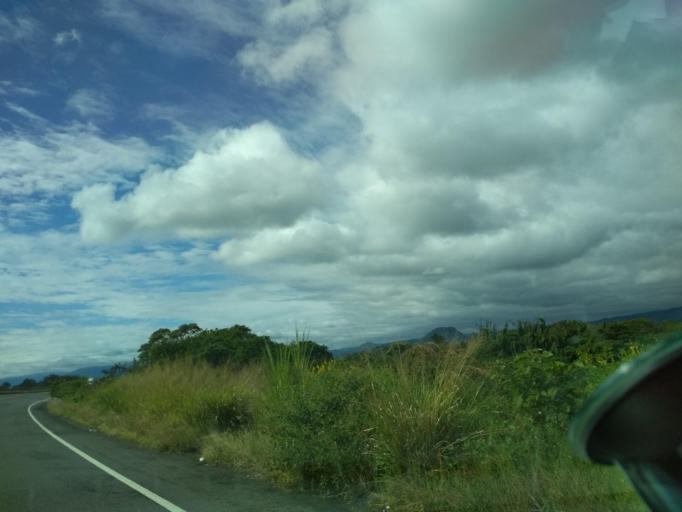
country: MX
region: Veracruz
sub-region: Coatepec
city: Las Lomas
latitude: 19.4478
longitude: -96.9276
